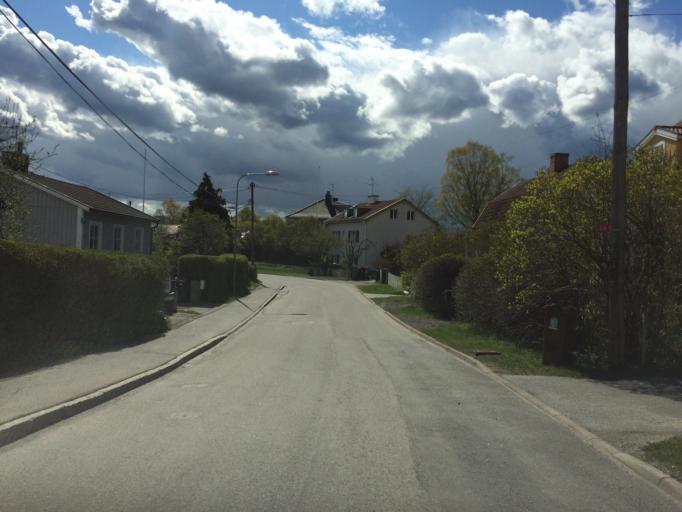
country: SE
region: Stockholm
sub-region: Huddinge Kommun
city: Segeltorp
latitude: 59.2923
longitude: 17.9546
